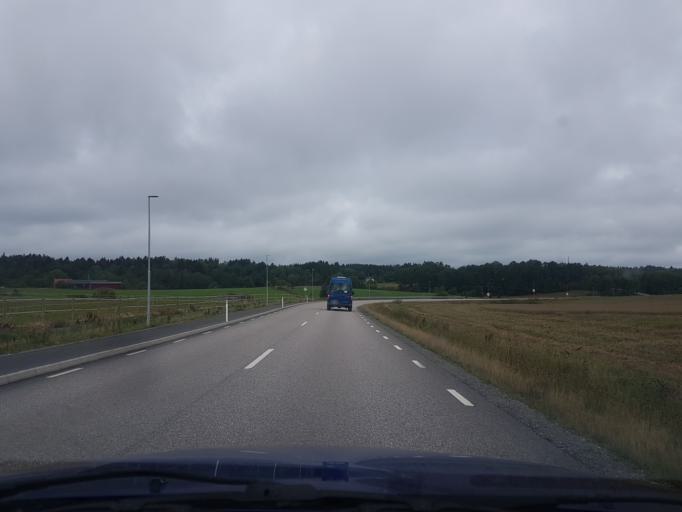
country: SE
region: Vaestra Goetaland
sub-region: Ale Kommun
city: Alvangen
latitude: 57.9417
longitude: 12.1423
